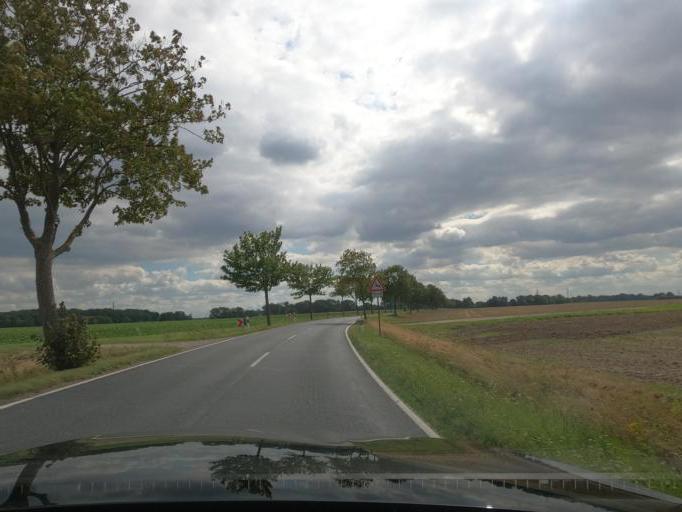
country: DE
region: Lower Saxony
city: Lehrte
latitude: 52.3522
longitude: 10.0276
